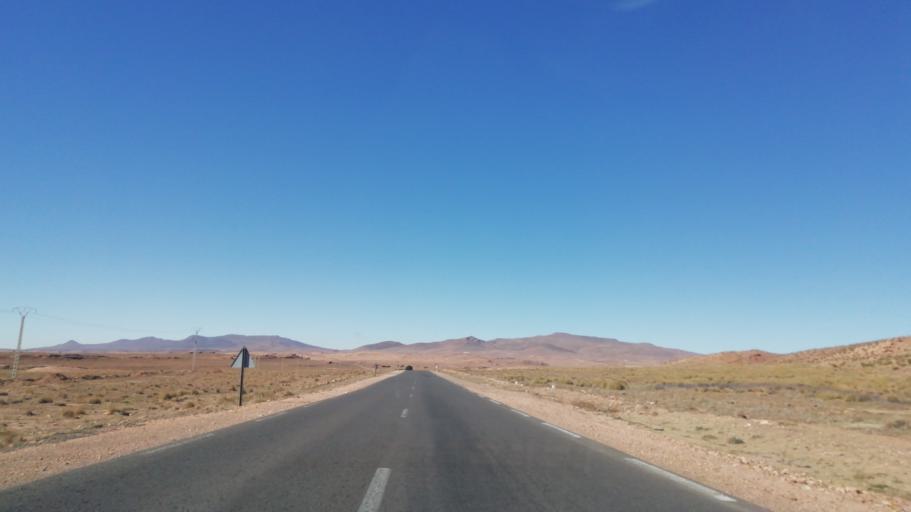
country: DZ
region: El Bayadh
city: El Bayadh
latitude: 33.6114
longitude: 1.2269
